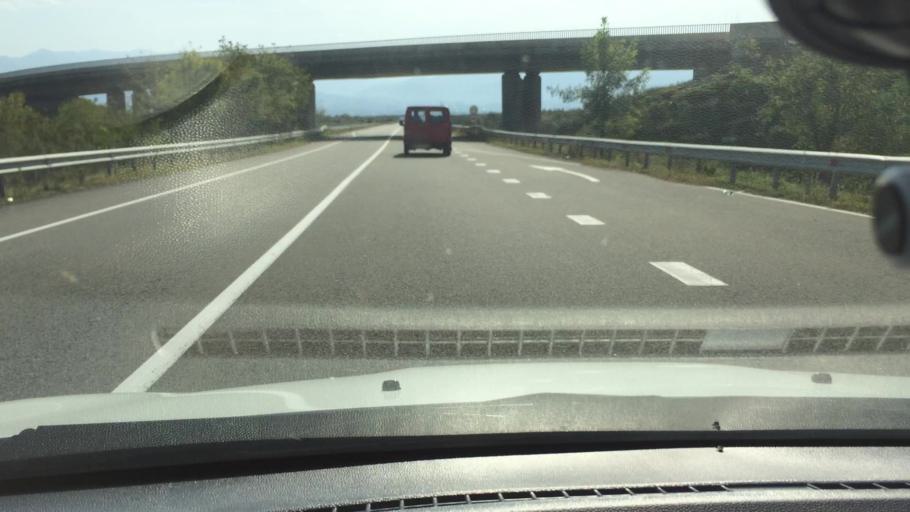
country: GE
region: Ajaria
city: Ochkhamuri
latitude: 41.8993
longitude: 41.7964
